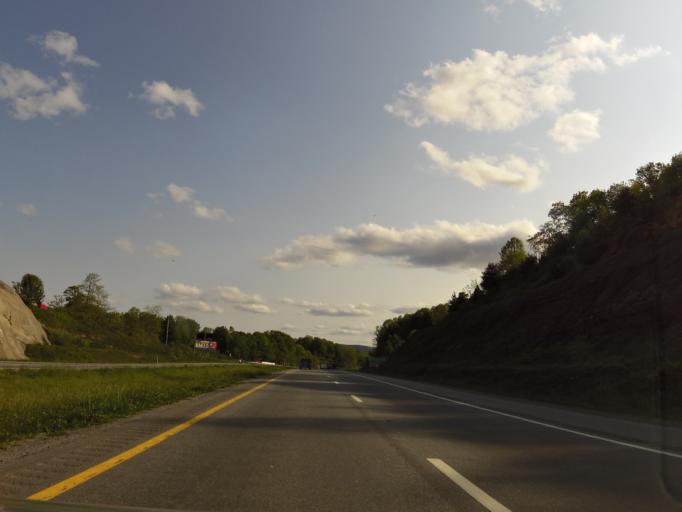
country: US
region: West Virginia
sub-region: Mercer County
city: Princeton
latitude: 37.3311
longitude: -81.1297
